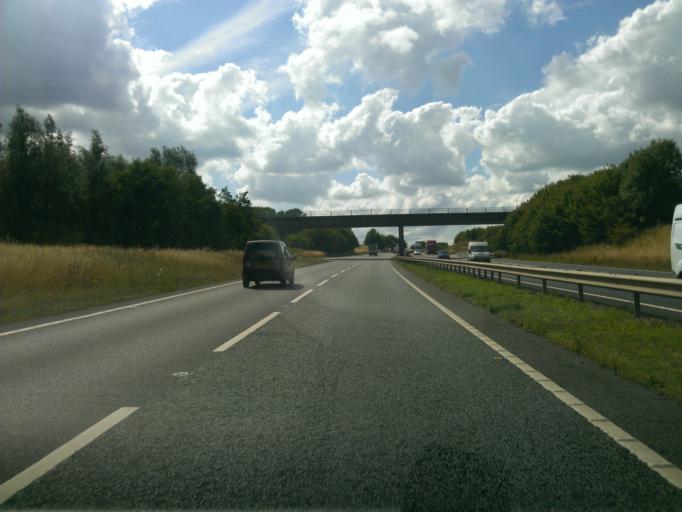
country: GB
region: England
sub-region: Northamptonshire
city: Brixworth
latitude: 52.3999
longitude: -0.9140
